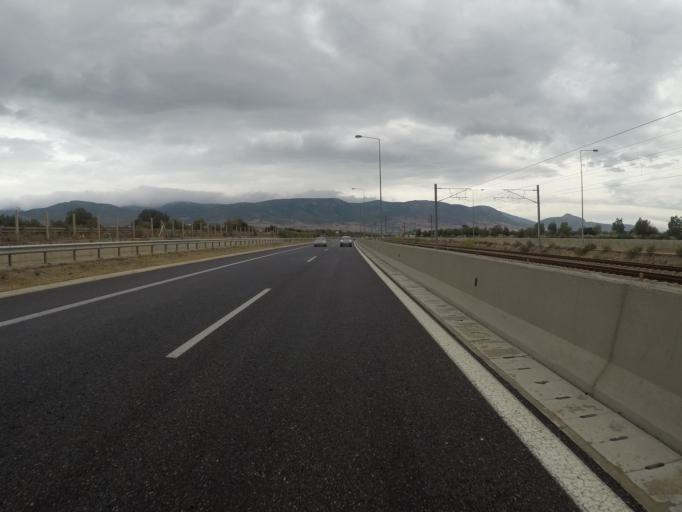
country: GR
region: Attica
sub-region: Nomarchia Dytikis Attikis
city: Magoula
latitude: 38.0861
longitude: 23.5433
